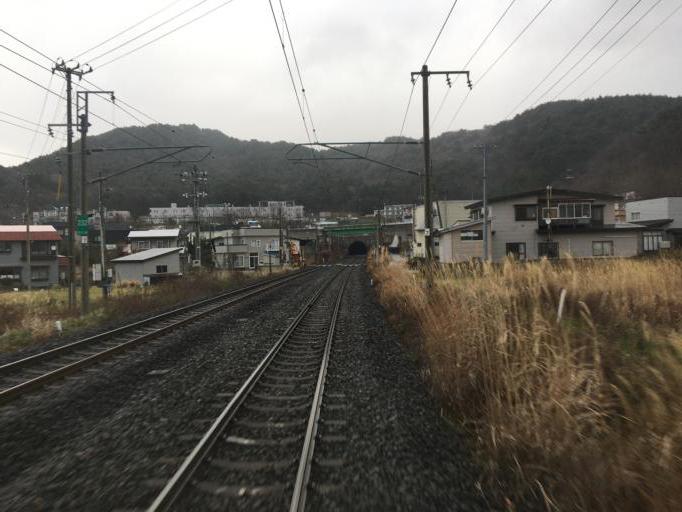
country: JP
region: Aomori
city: Aomori Shi
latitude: 40.8747
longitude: 140.8495
